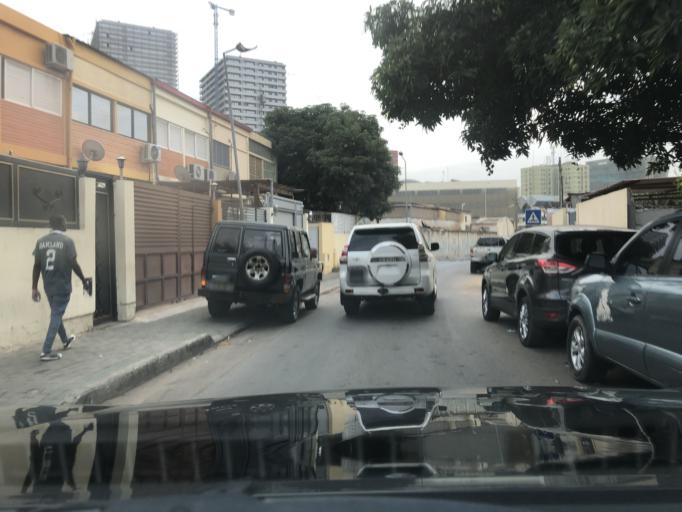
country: AO
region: Luanda
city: Luanda
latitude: -8.8269
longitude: 13.2529
